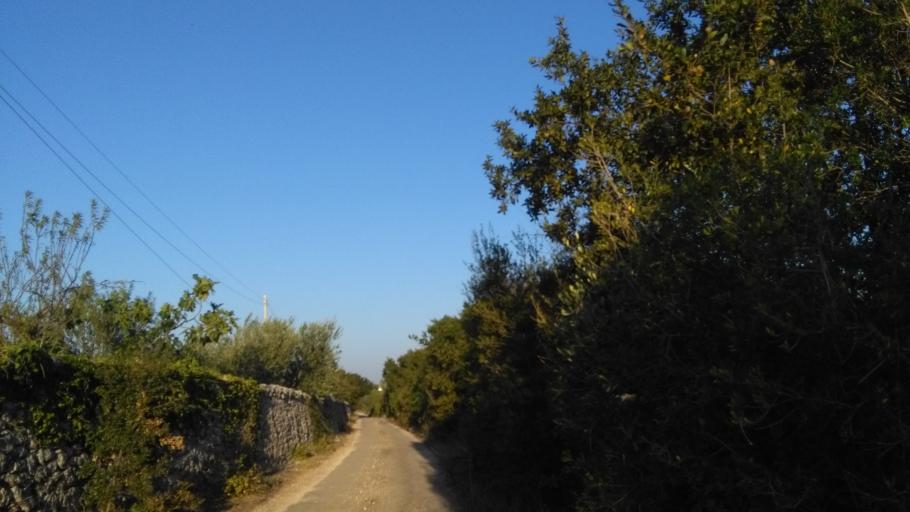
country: IT
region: Apulia
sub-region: Provincia di Bari
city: Putignano
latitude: 40.8312
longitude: 17.0686
